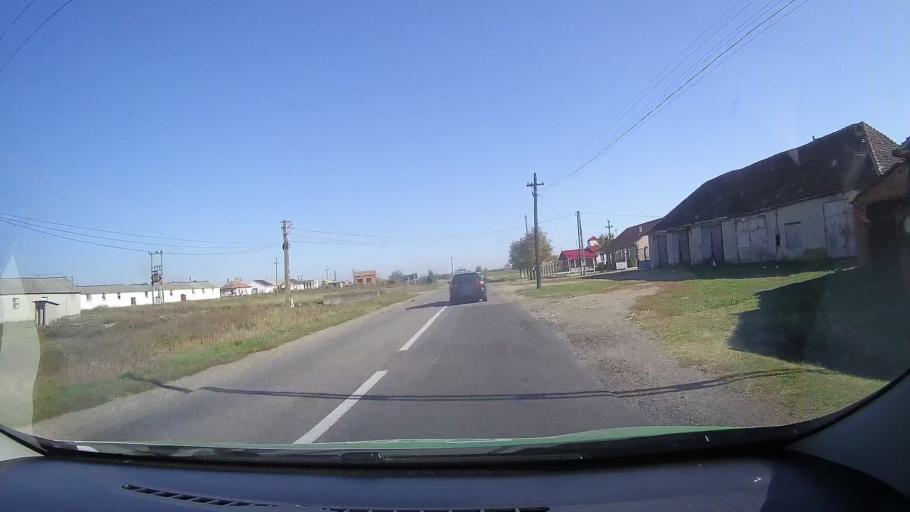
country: RO
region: Satu Mare
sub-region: Comuna Cauas
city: Cauas
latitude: 47.5726
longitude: 22.5475
